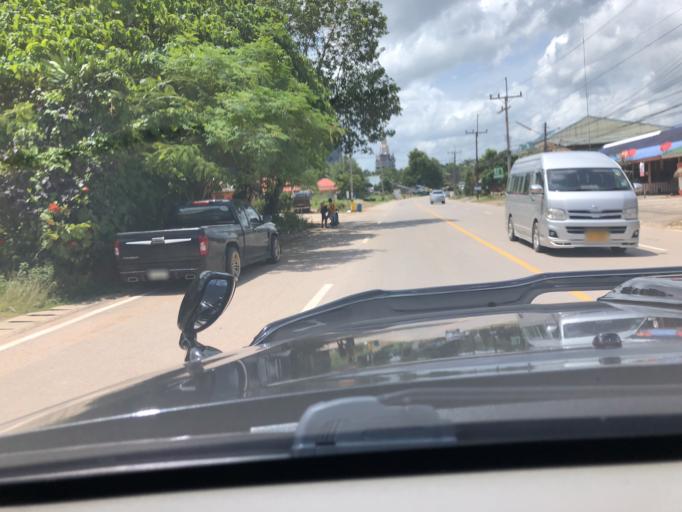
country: TH
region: Krabi
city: Krabi
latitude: 8.1172
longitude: 98.9233
